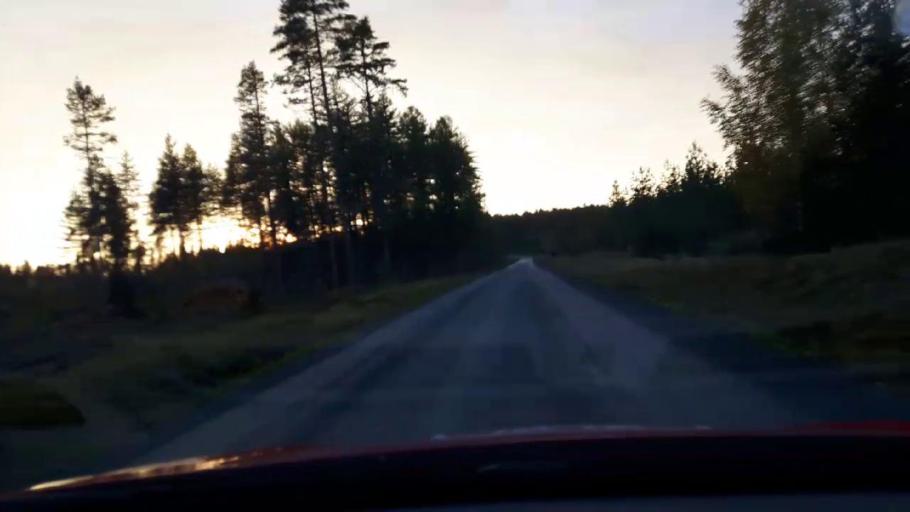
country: SE
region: Jaemtland
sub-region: OEstersunds Kommun
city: Lit
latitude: 63.2905
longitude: 14.8239
